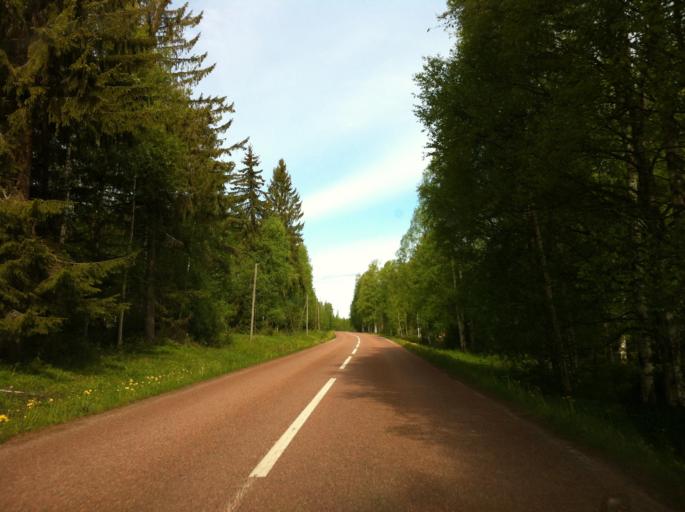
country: SE
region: Dalarna
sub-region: Mora Kommun
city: Mora
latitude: 60.8455
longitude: 14.6417
